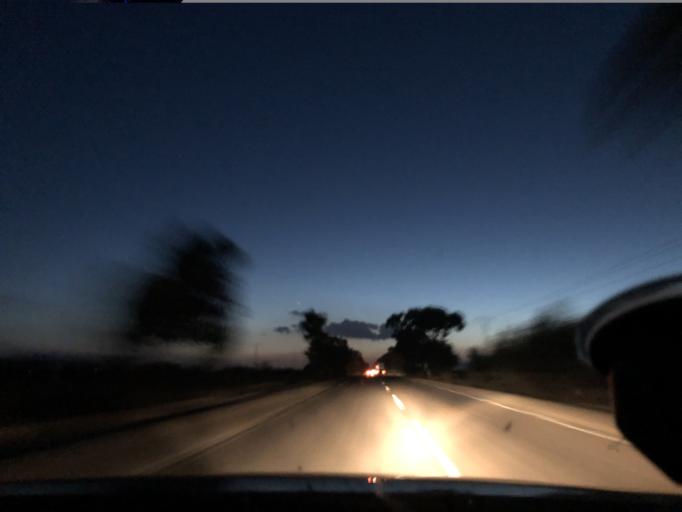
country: TN
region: Al Qasrayn
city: Kasserine
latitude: 35.2311
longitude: 8.9634
